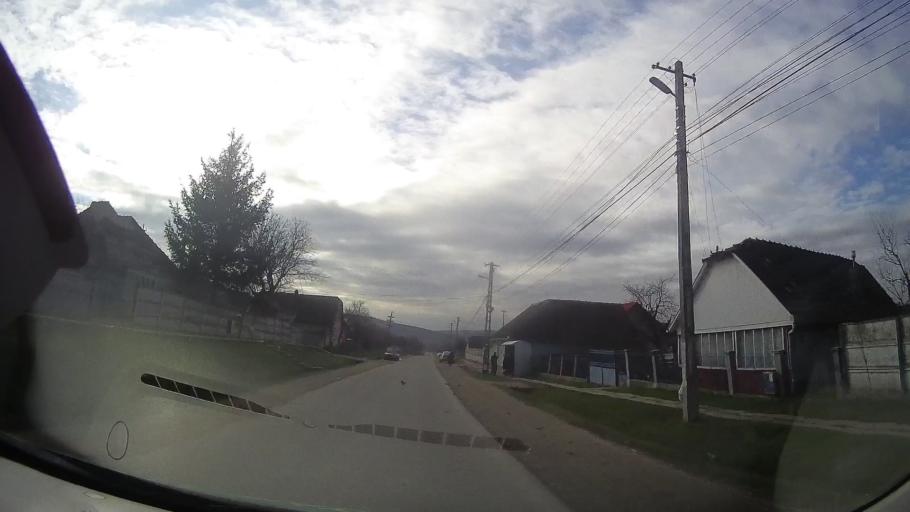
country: RO
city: Barza
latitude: 46.5555
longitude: 24.1323
